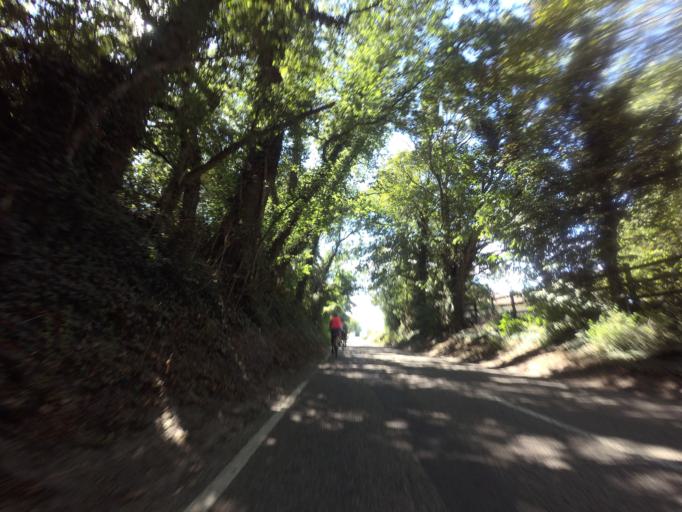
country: GB
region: England
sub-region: Kent
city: Birchington-on-Sea
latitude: 51.3356
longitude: 1.3251
